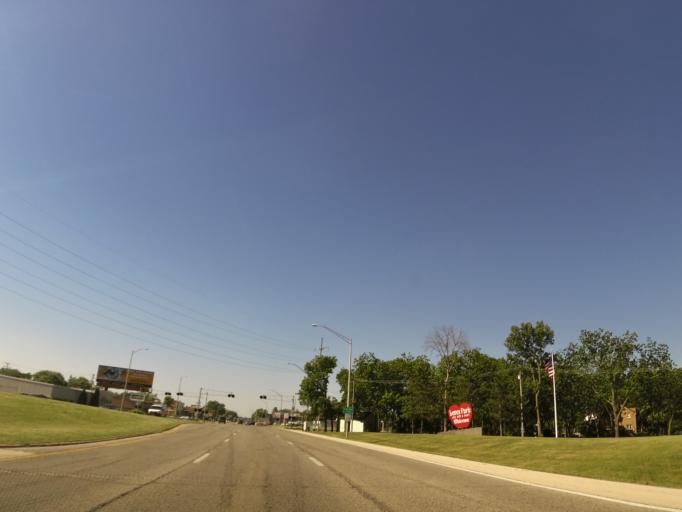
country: US
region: Illinois
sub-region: Winnebago County
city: Loves Park
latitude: 42.2966
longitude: -89.0575
